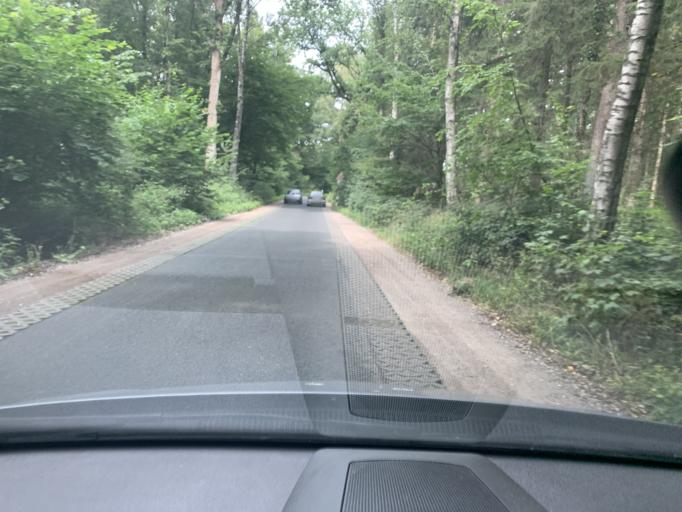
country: DE
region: Schleswig-Holstein
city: Guster
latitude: 53.5520
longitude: 10.6937
